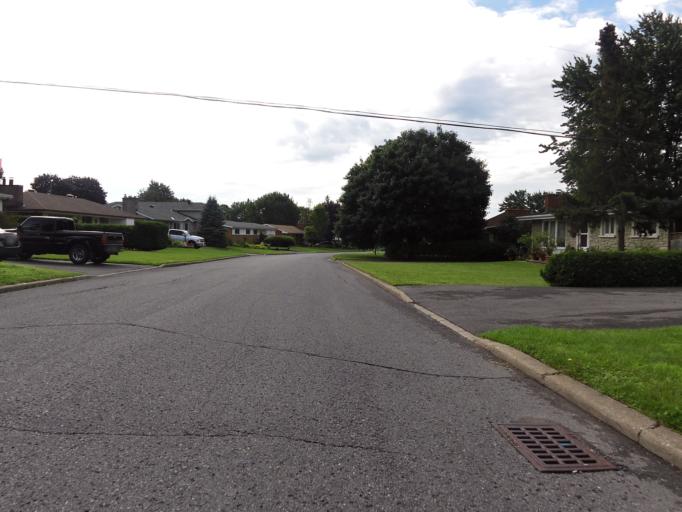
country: CA
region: Ontario
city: Ottawa
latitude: 45.3442
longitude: -75.7343
